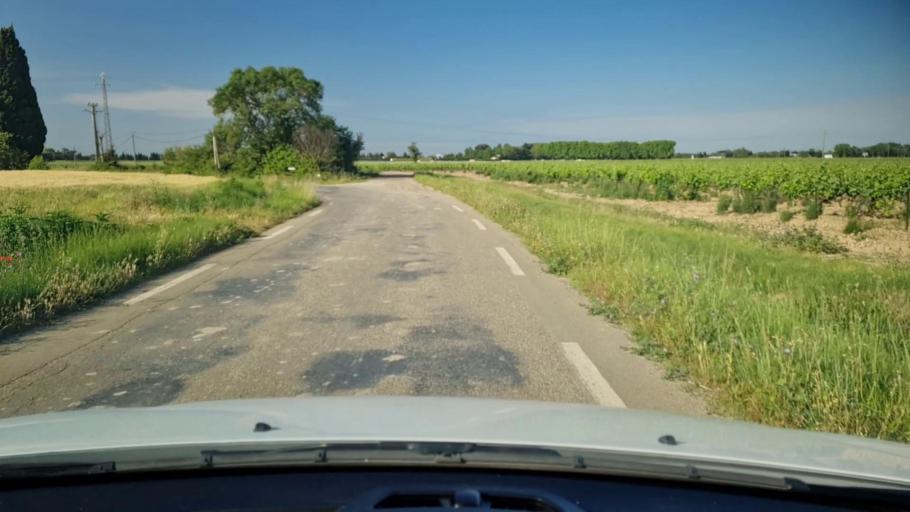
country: FR
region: Languedoc-Roussillon
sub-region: Departement du Gard
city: Aimargues
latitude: 43.6664
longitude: 4.2141
